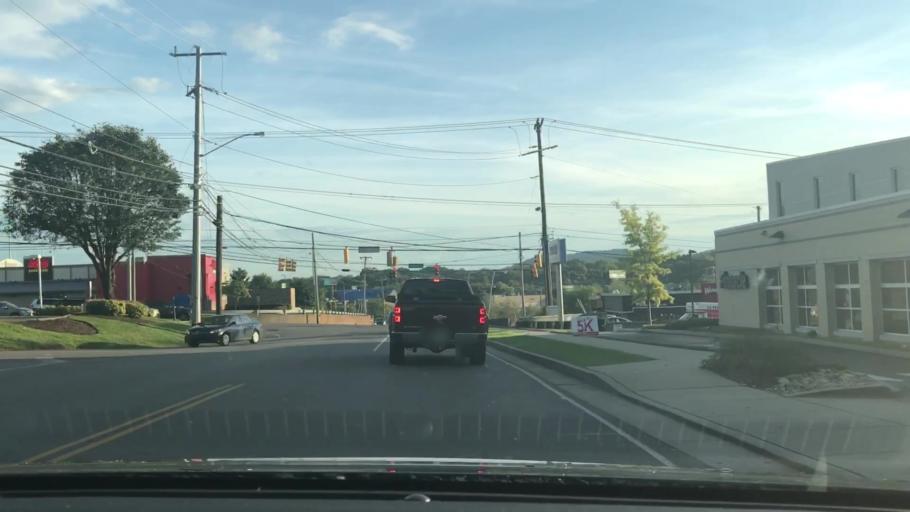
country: US
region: Tennessee
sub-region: Davidson County
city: Oak Hill
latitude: 36.1130
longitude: -86.7670
